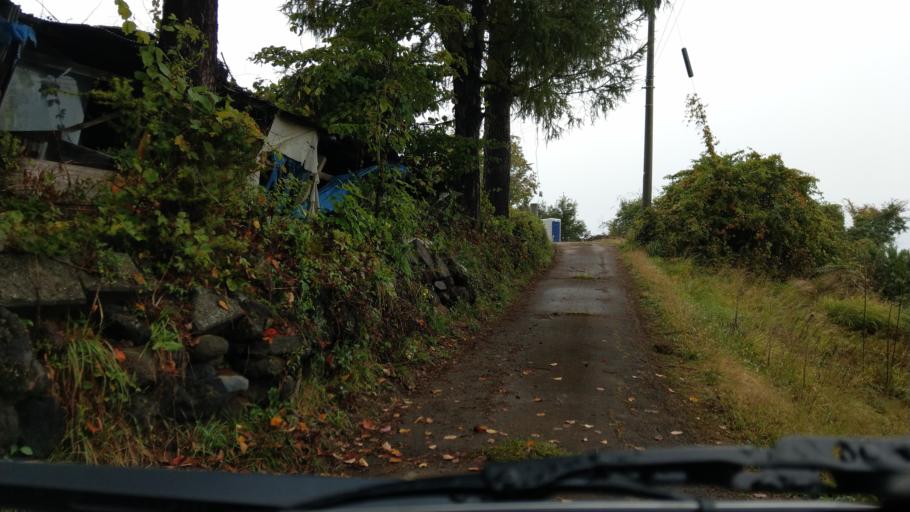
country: JP
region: Nagano
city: Komoro
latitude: 36.3591
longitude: 138.4449
